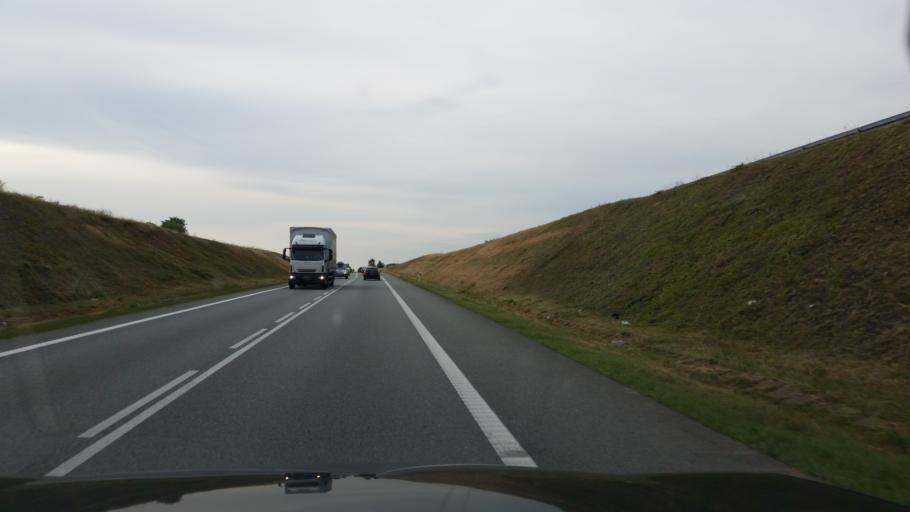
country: PL
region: Silesian Voivodeship
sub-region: Powiat bedzinski
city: Mierzecice
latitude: 50.4400
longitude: 19.1461
